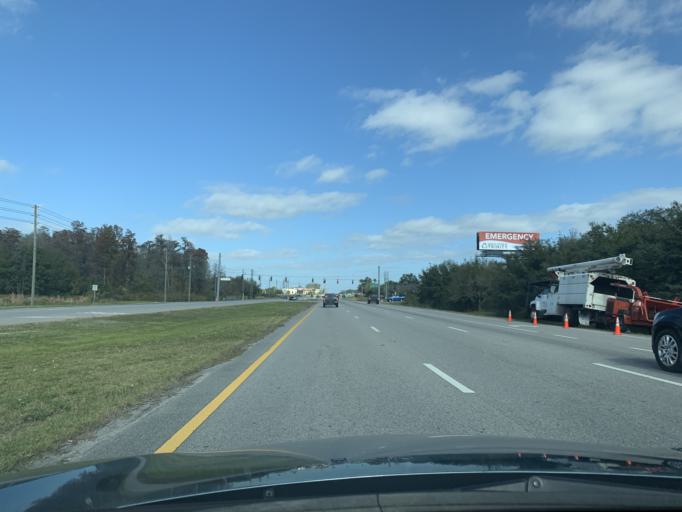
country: US
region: Florida
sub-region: Pasco County
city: Trinity
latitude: 28.1989
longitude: -82.6664
